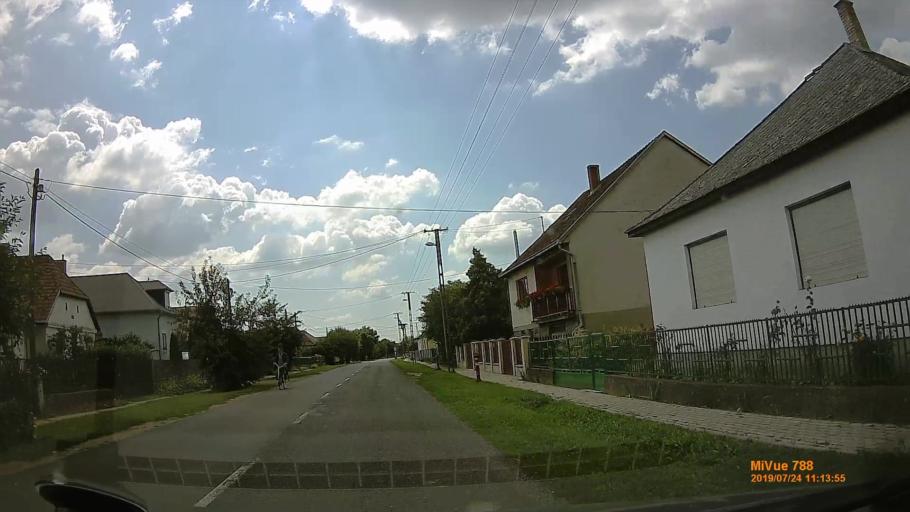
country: HU
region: Szabolcs-Szatmar-Bereg
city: Tarpa
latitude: 48.1991
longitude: 22.4460
